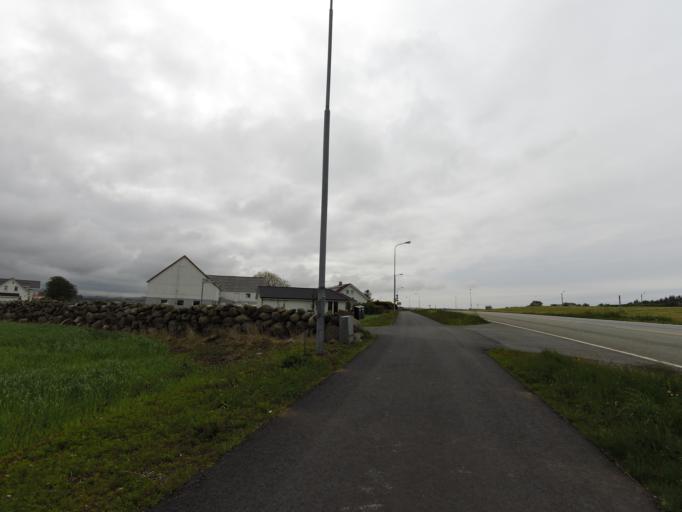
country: NO
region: Rogaland
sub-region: Klepp
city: Kleppe
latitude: 58.8254
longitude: 5.5893
